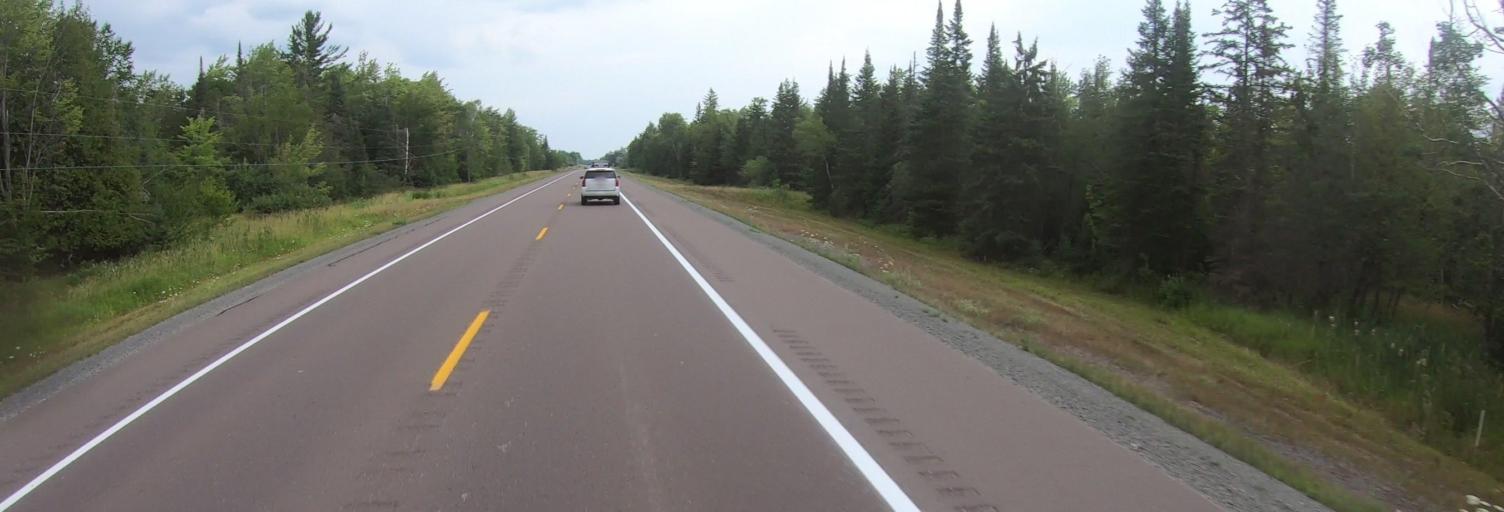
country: US
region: Michigan
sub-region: Baraga County
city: Baraga
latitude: 46.9279
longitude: -88.4591
